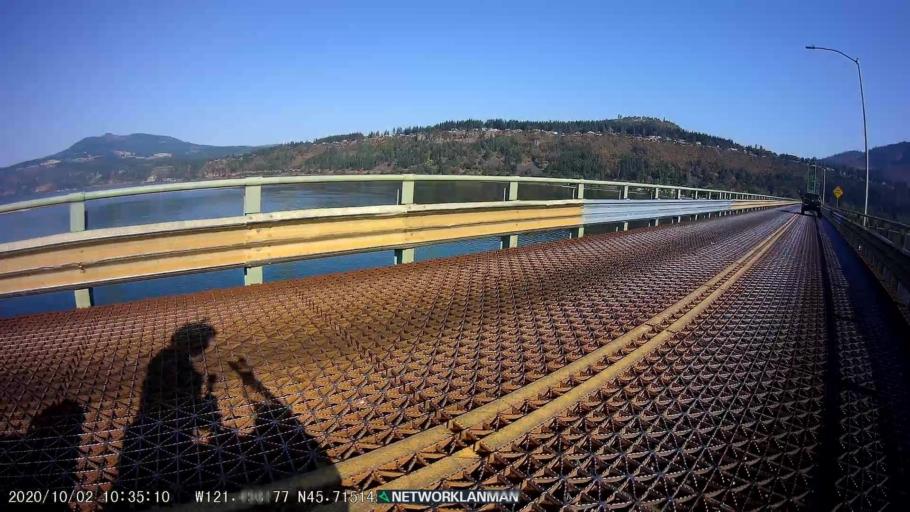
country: US
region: Washington
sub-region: Klickitat County
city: White Salmon
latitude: 45.7151
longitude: -121.4993
